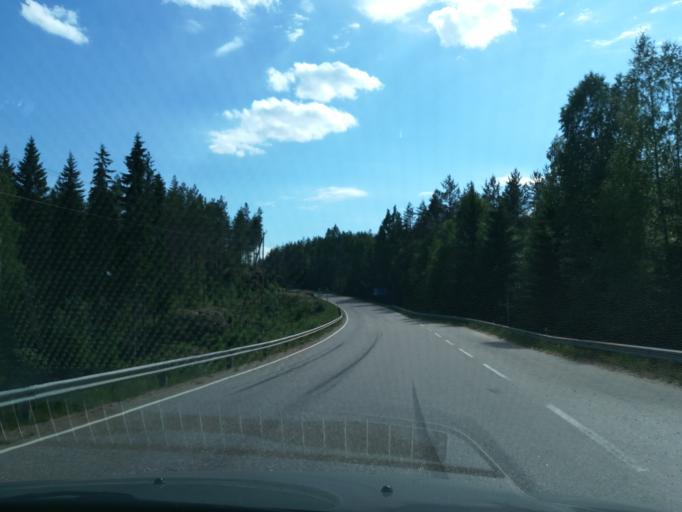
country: FI
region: South Karelia
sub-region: Imatra
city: Ruokolahti
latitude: 61.4783
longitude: 28.7887
